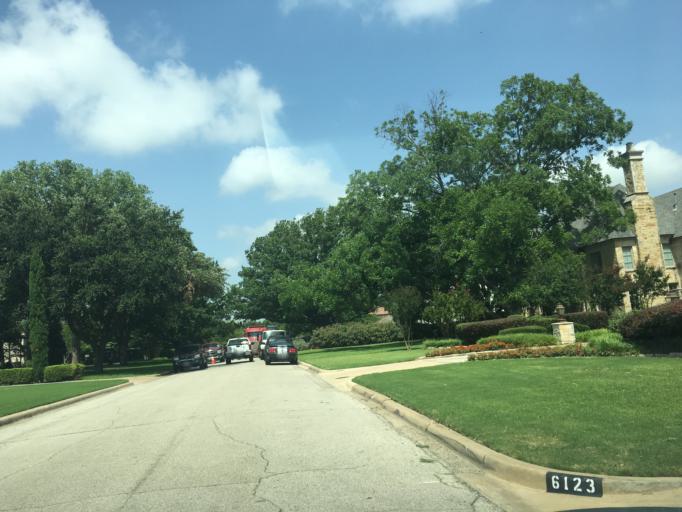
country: US
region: Texas
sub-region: Dallas County
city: University Park
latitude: 32.8782
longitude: -96.8010
